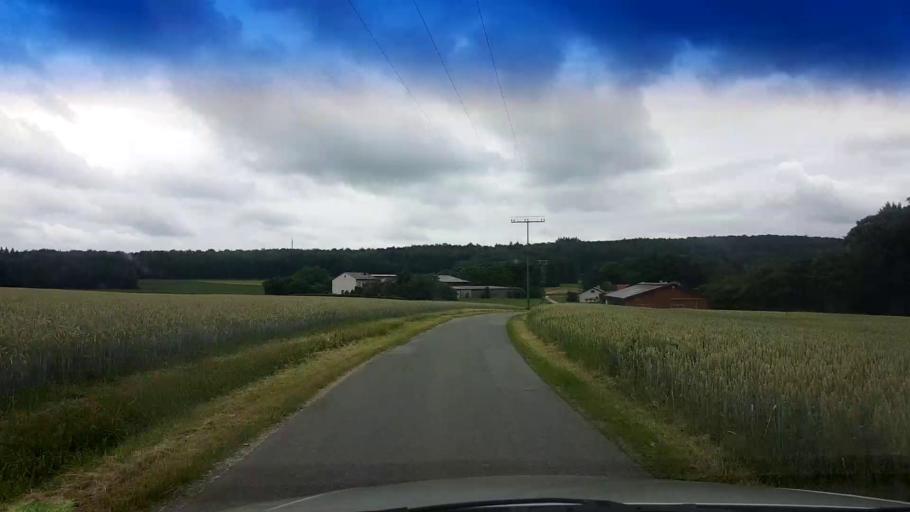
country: DE
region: Bavaria
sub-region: Upper Franconia
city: Poxdorf
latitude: 49.9048
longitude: 11.0834
